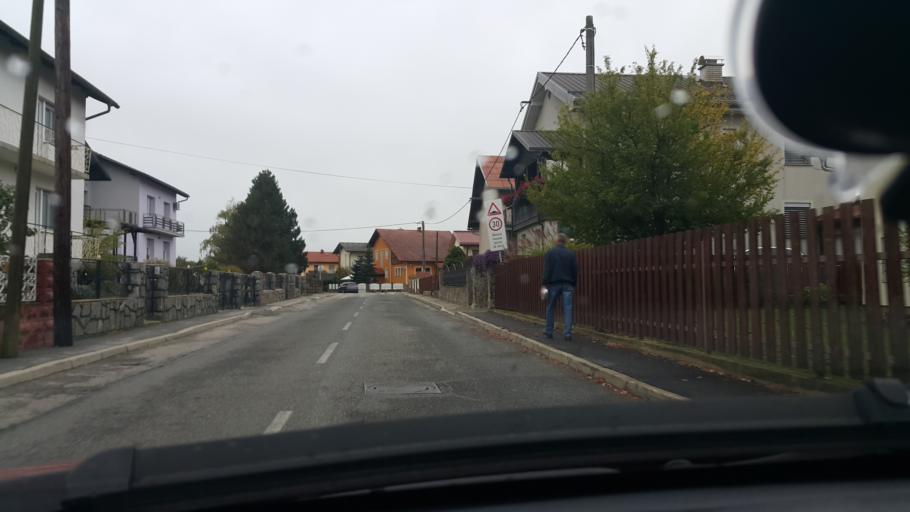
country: SI
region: Hoce-Slivnica
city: Rogoza
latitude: 46.5328
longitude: 15.6756
